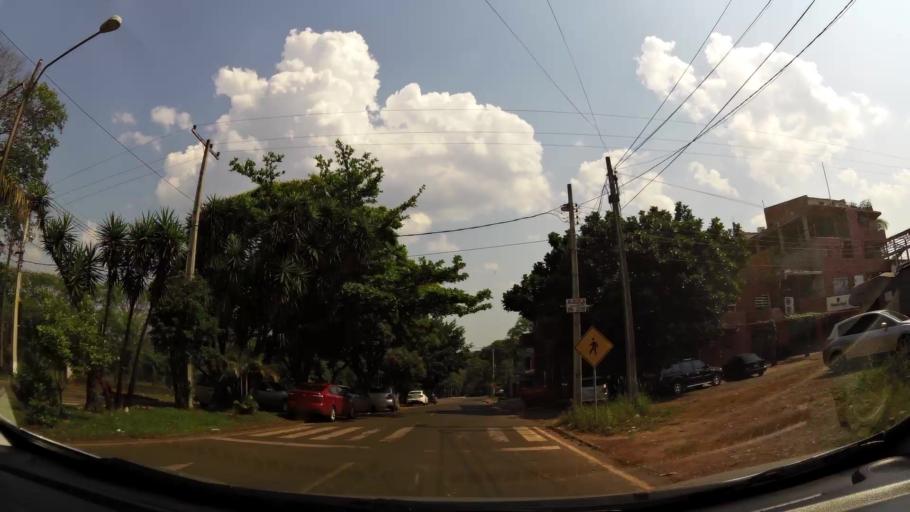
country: PY
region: Alto Parana
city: Ciudad del Este
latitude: -25.5119
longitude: -54.6348
